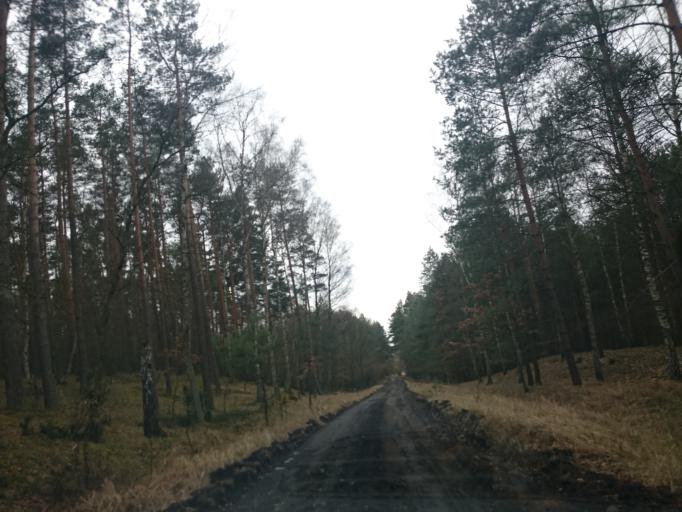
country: PL
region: Kujawsko-Pomorskie
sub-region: Powiat golubsko-dobrzynski
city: Ciechocin
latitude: 53.0732
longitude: 18.9033
